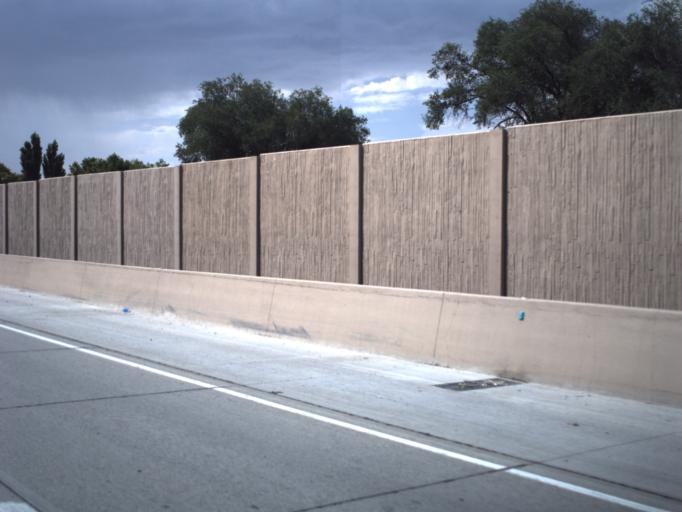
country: US
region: Utah
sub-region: Salt Lake County
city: South Salt Lake
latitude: 40.7184
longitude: -111.8799
